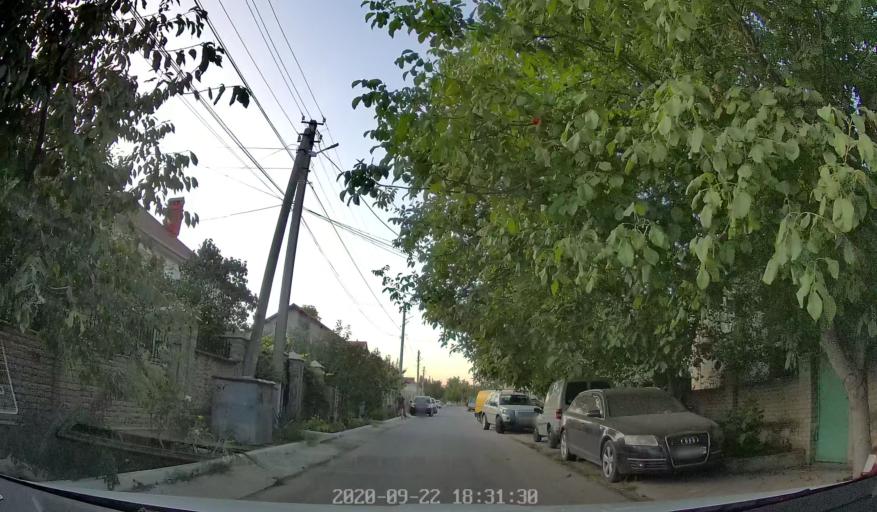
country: MD
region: Laloveni
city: Ialoveni
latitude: 46.9594
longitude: 28.7595
